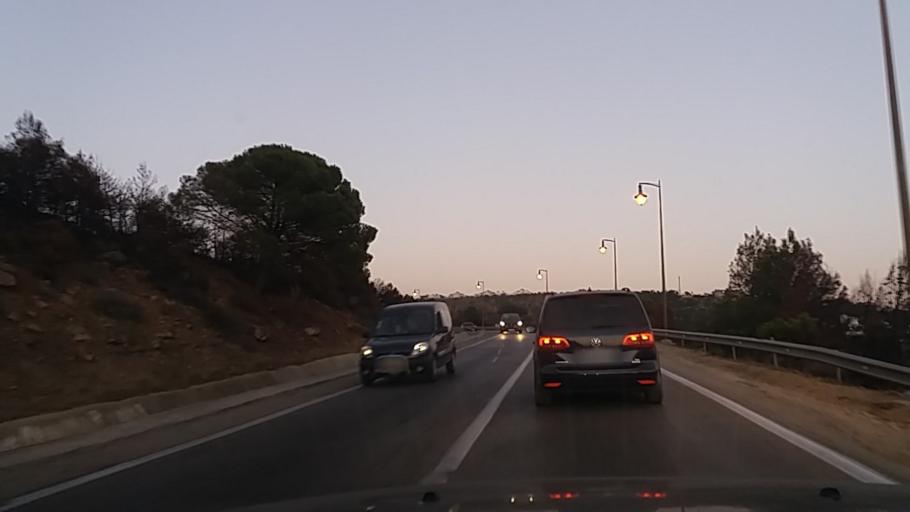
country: MA
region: Tanger-Tetouan
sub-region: Tanger-Assilah
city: Boukhalef
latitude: 35.7774
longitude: -5.9199
